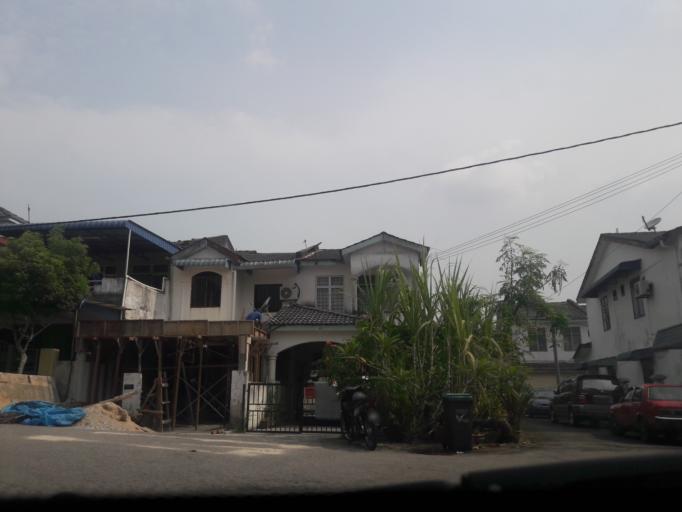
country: MY
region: Kedah
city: Kulim
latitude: 5.3647
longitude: 100.5377
